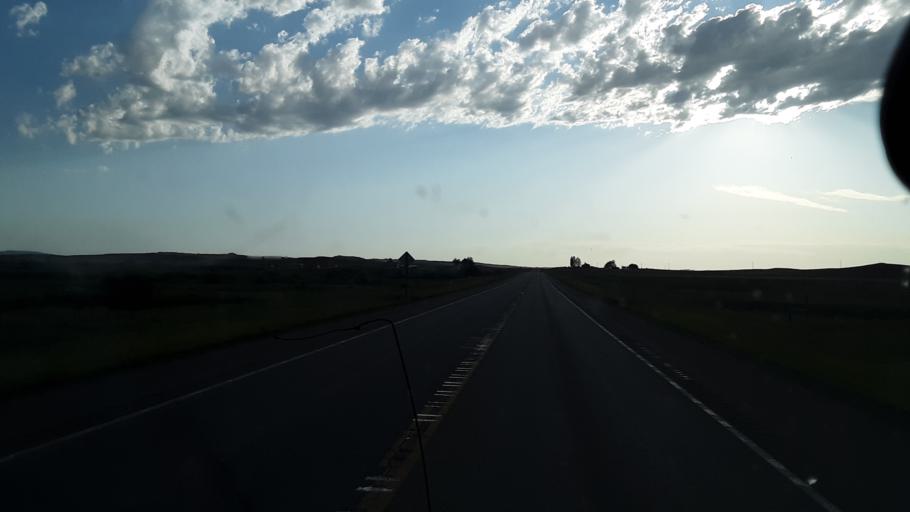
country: US
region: Montana
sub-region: Rosebud County
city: Lame Deer
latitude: 45.5285
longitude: -106.9666
